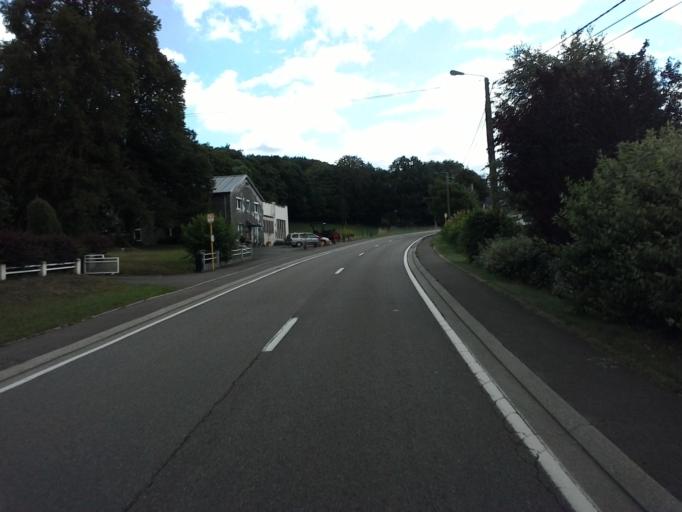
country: BE
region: Wallonia
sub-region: Province du Luxembourg
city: Leglise
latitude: 49.8009
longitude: 5.5443
